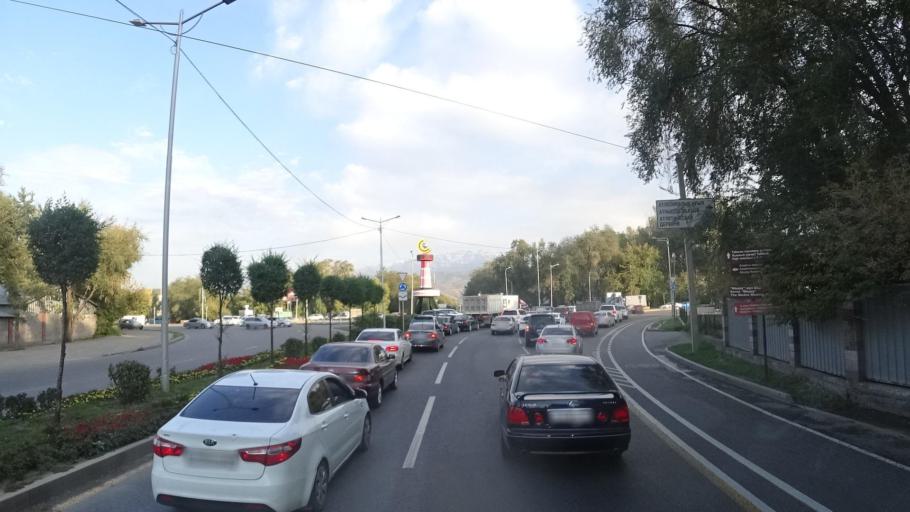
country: KZ
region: Almaty Oblysy
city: Pervomayskiy
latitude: 43.3203
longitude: 77.0247
